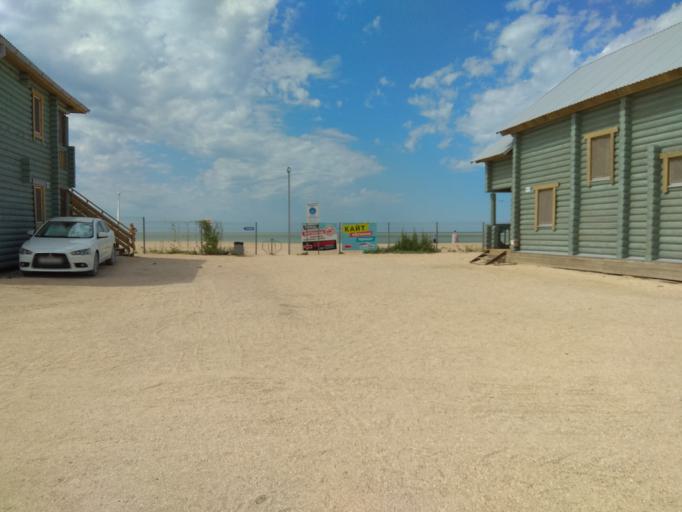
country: RU
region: Krasnodarskiy
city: Dolzhanskaya
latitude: 46.6802
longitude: 37.7381
